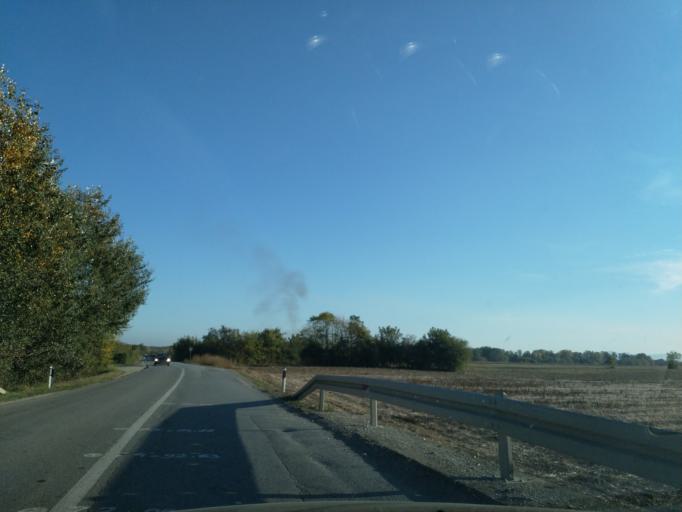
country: RS
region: Central Serbia
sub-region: Pomoravski Okrug
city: Svilajnac
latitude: 44.2361
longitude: 21.1367
